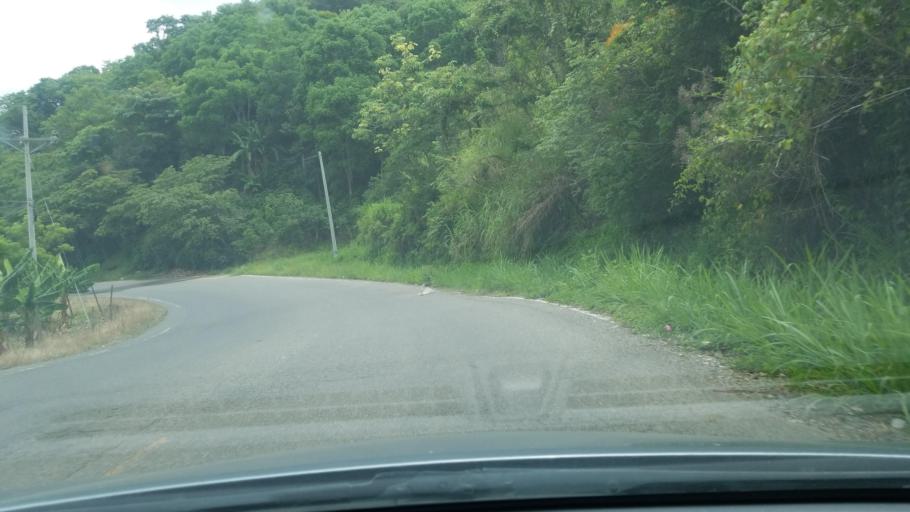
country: HN
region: Copan
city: Ojos de Agua
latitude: 14.6748
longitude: -88.8269
